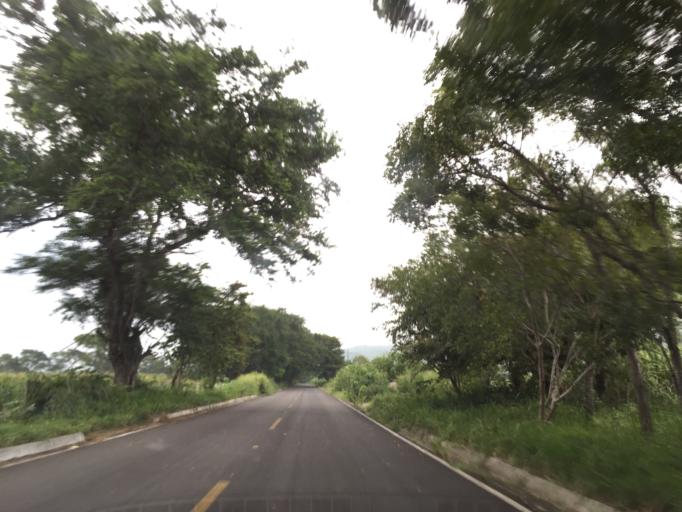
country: MX
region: Colima
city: Comala
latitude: 19.3802
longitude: -103.8028
